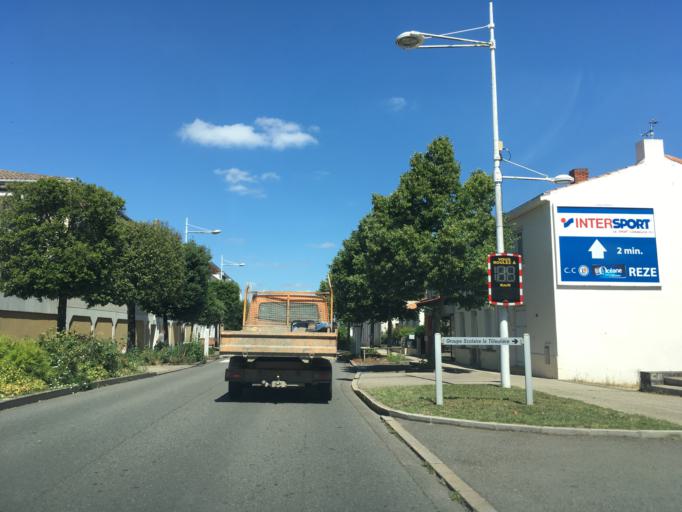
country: FR
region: Pays de la Loire
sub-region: Departement de la Loire-Atlantique
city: Les Sorinieres
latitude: 47.1468
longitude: -1.5293
